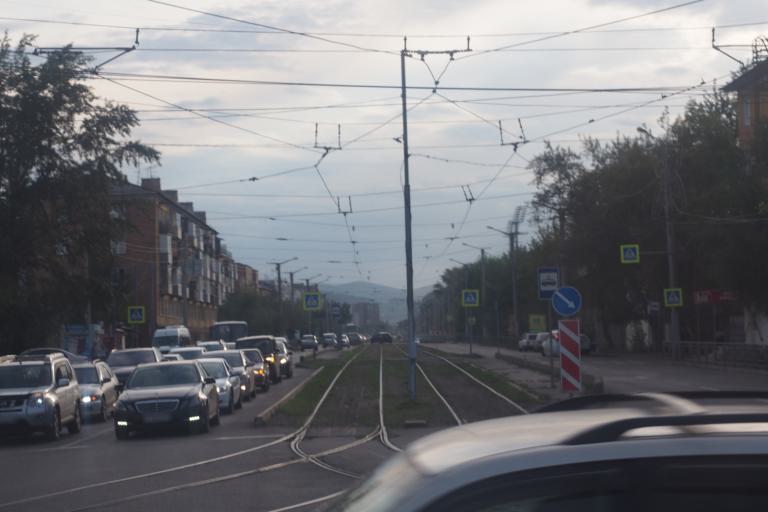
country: RU
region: Krasnoyarskiy
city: Krasnoyarsk
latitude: 55.9952
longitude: 92.9714
